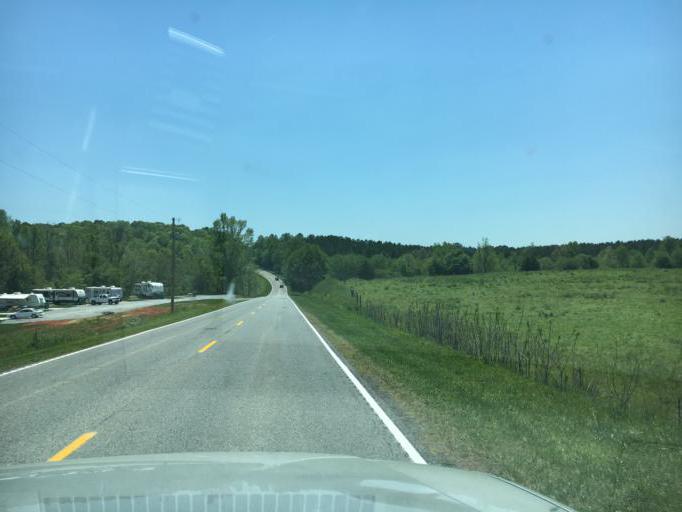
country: US
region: South Carolina
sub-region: Cherokee County
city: Blacksburg
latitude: 35.1604
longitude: -81.5752
